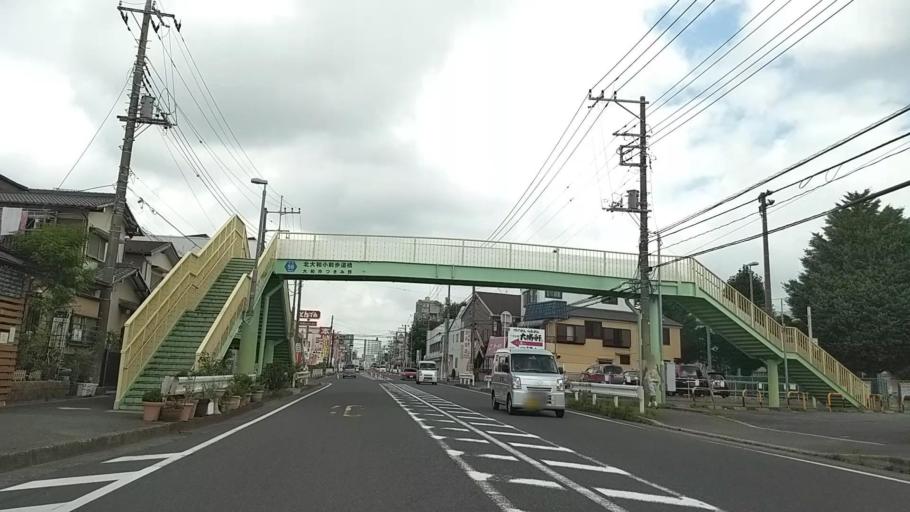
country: JP
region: Kanagawa
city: Minami-rinkan
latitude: 35.5081
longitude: 139.4618
